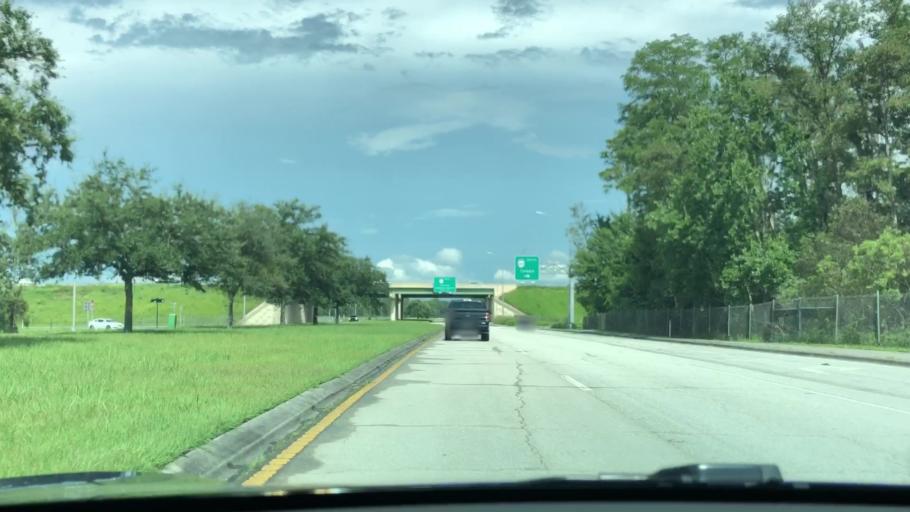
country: US
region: Florida
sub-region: Orange County
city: Azalea Park
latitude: 28.4777
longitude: -81.2416
